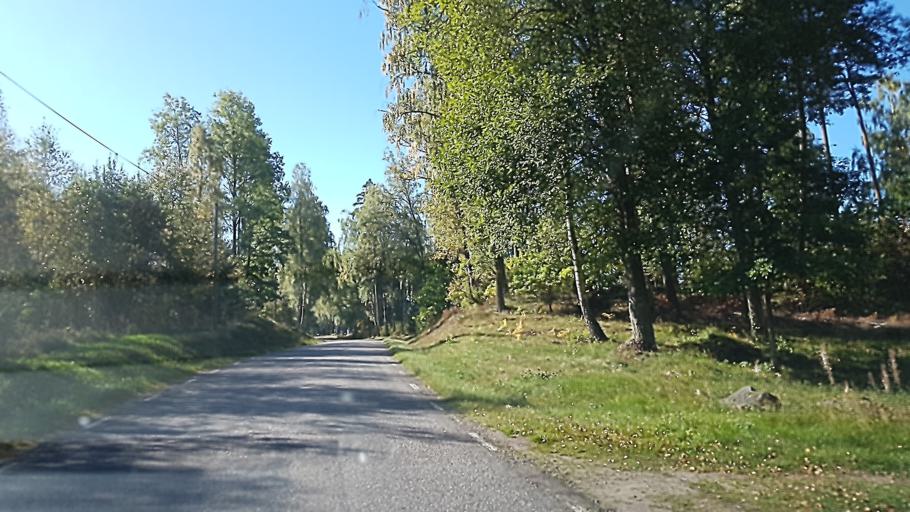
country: SE
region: Kronoberg
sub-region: Ljungby Kommun
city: Ljungby
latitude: 56.8022
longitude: 14.0333
